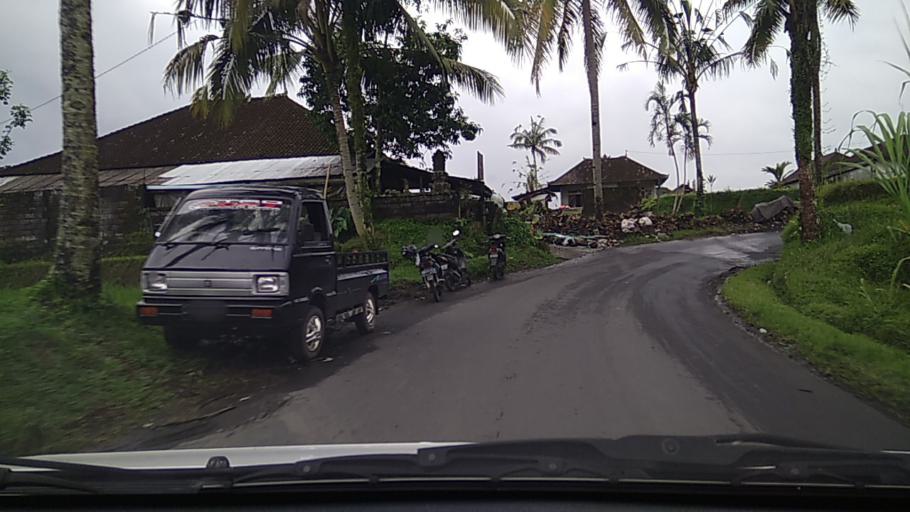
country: ID
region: Bali
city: Banjar Dujung Kaja
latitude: -8.4161
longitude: 115.2961
